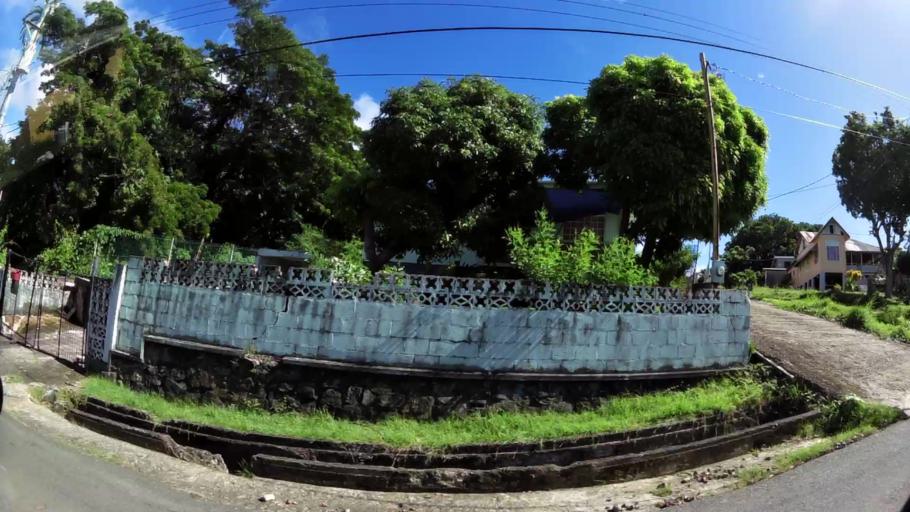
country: TT
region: Tobago
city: Scarborough
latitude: 11.1806
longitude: -60.7291
